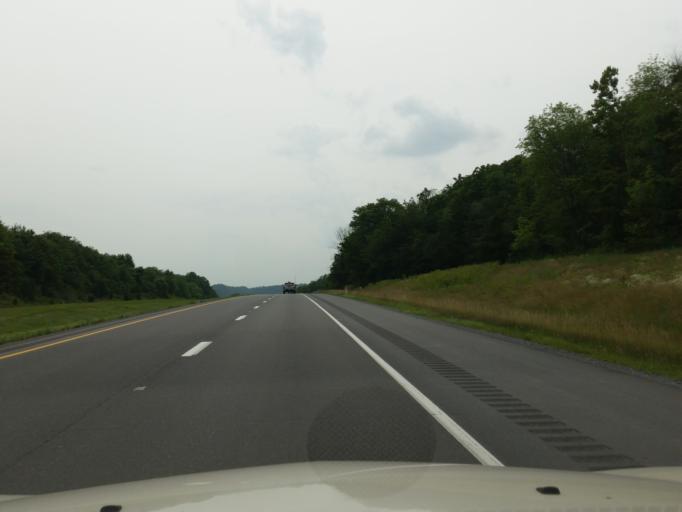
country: US
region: Pennsylvania
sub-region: Juniata County
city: Mifflintown
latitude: 40.5424
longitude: -77.3299
